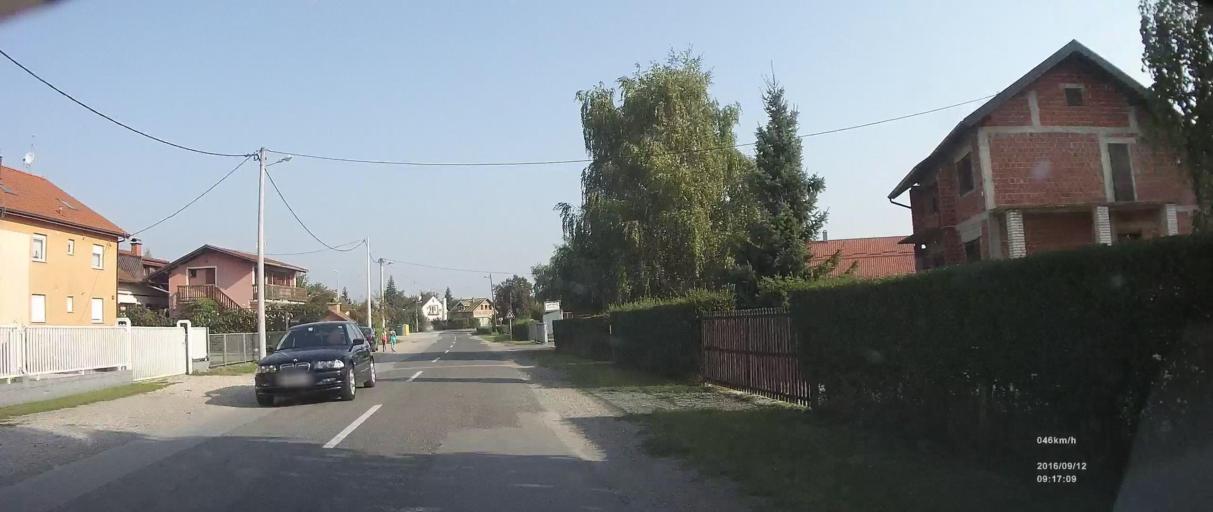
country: HR
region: Zagrebacka
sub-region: Grad Velika Gorica
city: Velika Gorica
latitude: 45.7025
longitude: 16.0669
